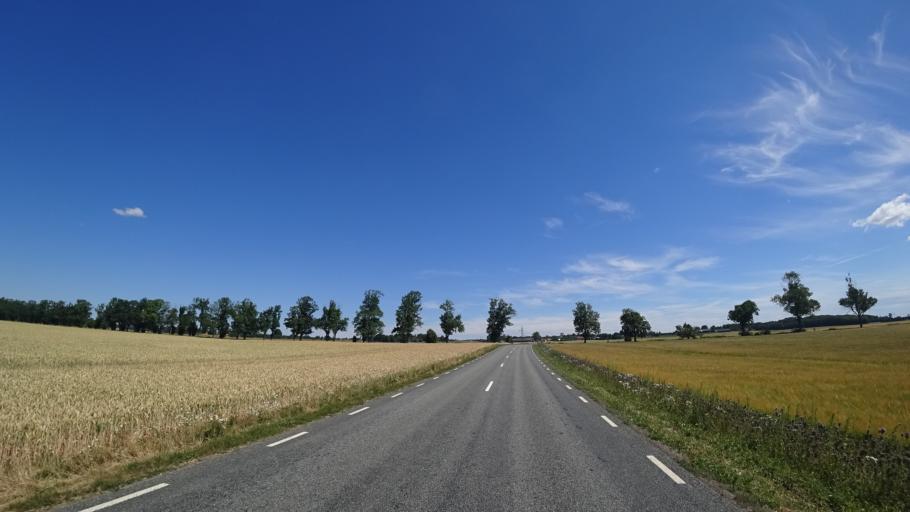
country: SE
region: Skane
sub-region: Kristianstads Kommun
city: Onnestad
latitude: 56.0682
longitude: 14.0624
